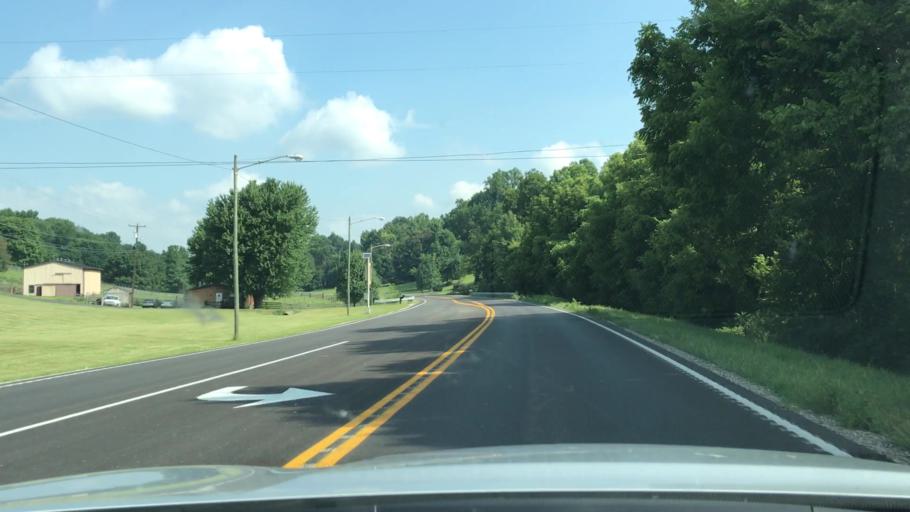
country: US
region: Kentucky
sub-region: Barren County
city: Glasgow
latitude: 37.0233
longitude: -85.9059
